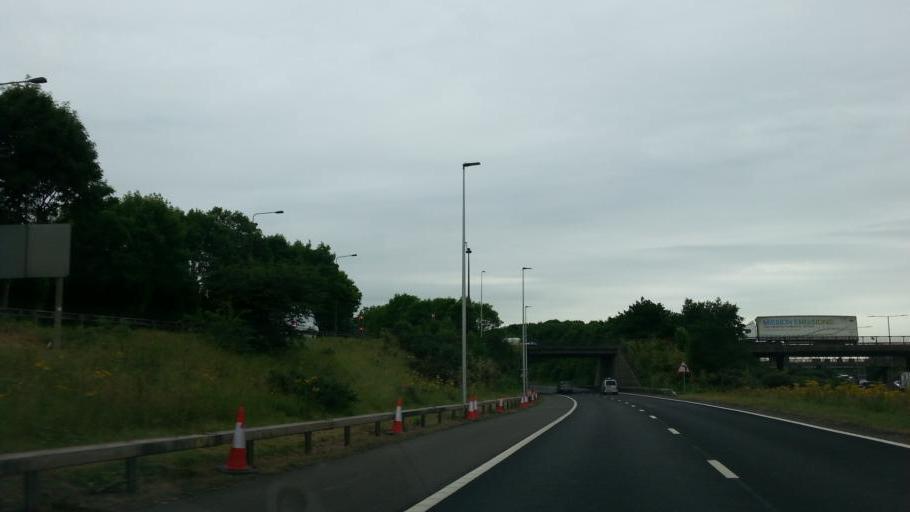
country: GB
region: England
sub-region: Solihull
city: Chelmsley Wood
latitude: 52.4762
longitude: -1.7045
